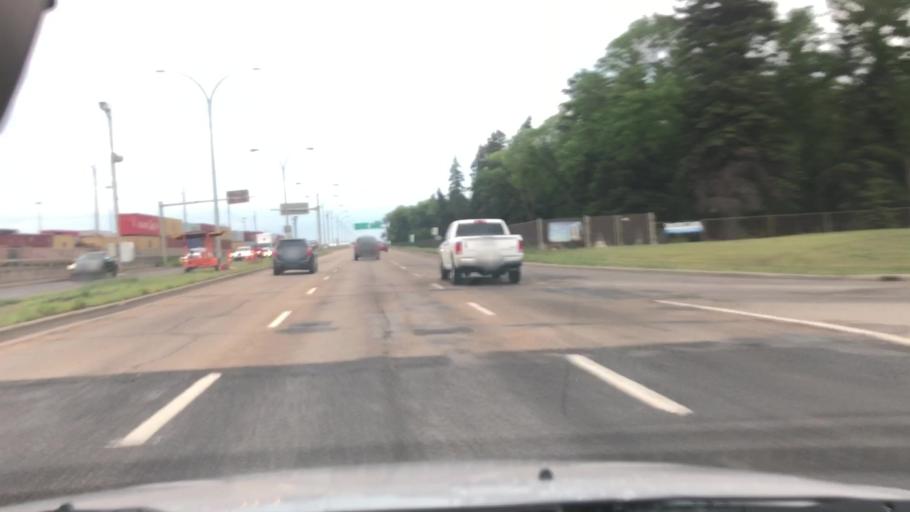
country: CA
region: Alberta
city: Edmonton
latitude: 53.5813
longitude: -113.5051
